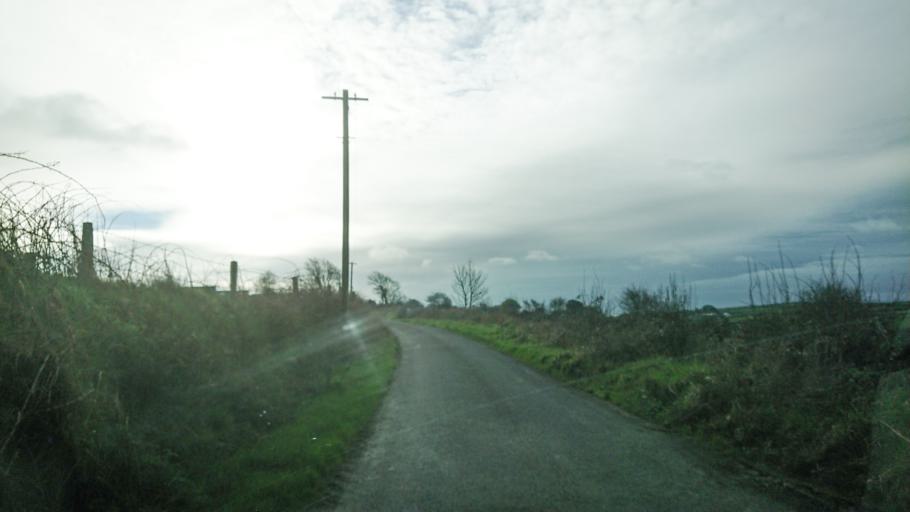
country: IE
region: Munster
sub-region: Waterford
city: Tra Mhor
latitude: 52.1511
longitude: -7.1925
